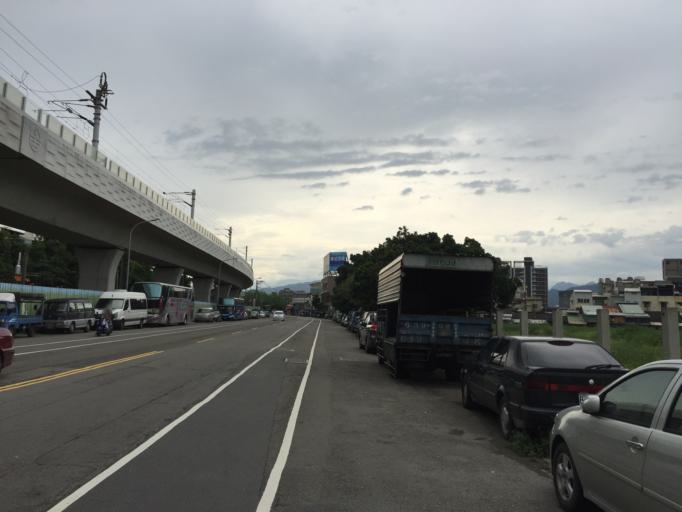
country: TW
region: Taiwan
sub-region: Taichung City
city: Taichung
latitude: 24.1395
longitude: 120.6926
